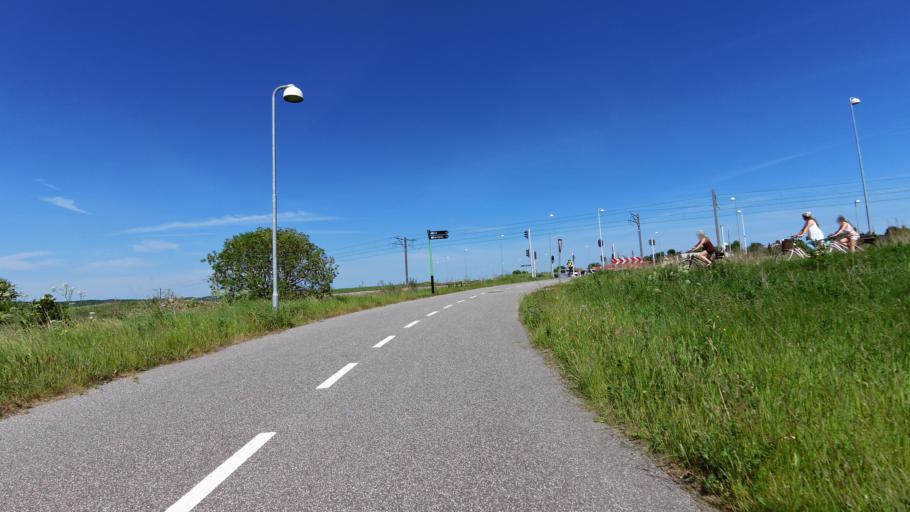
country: DK
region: Central Jutland
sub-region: Arhus Kommune
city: Trige
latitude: 56.1995
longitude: 10.1648
